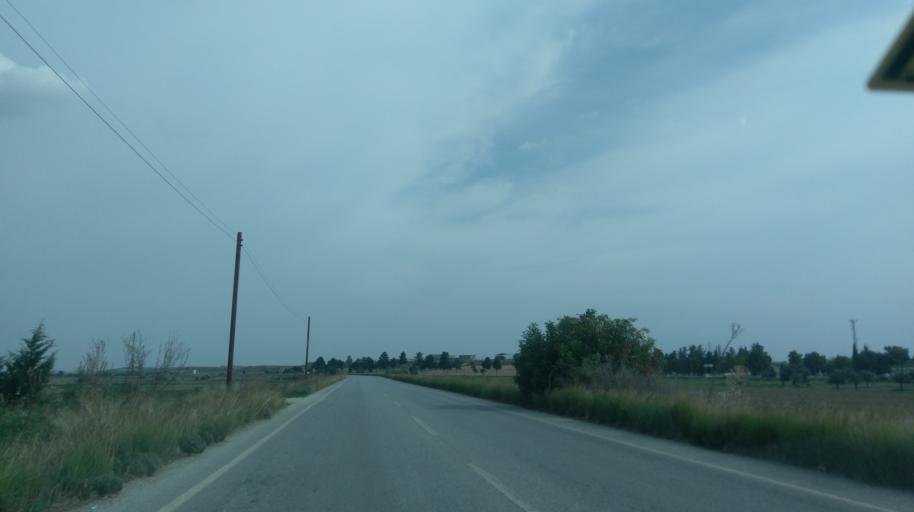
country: CY
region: Ammochostos
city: Lefkonoiko
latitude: 35.2634
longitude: 33.7912
